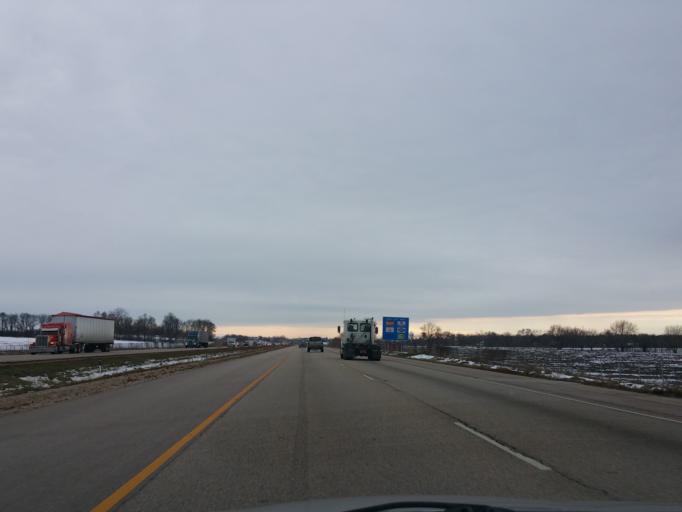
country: US
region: Wisconsin
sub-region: Rock County
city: Beloit
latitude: 42.5421
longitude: -88.9751
